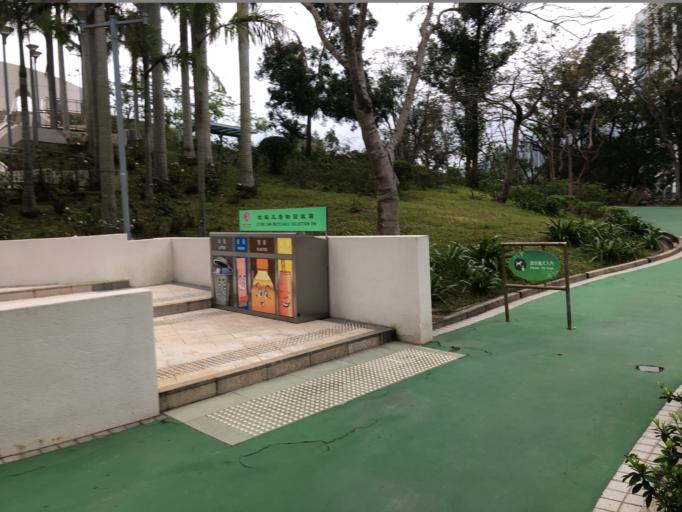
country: HK
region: Tai Po
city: Tai Po
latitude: 22.4505
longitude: 114.1757
